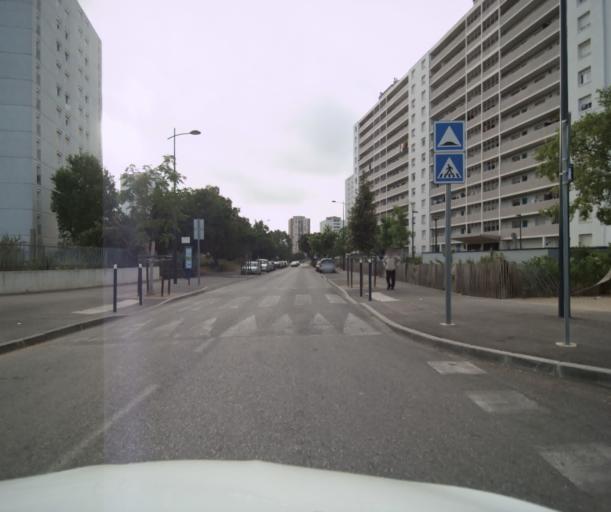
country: FR
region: Provence-Alpes-Cote d'Azur
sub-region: Departement du Var
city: Six-Fours-les-Plages
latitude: 43.1145
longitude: 5.8620
